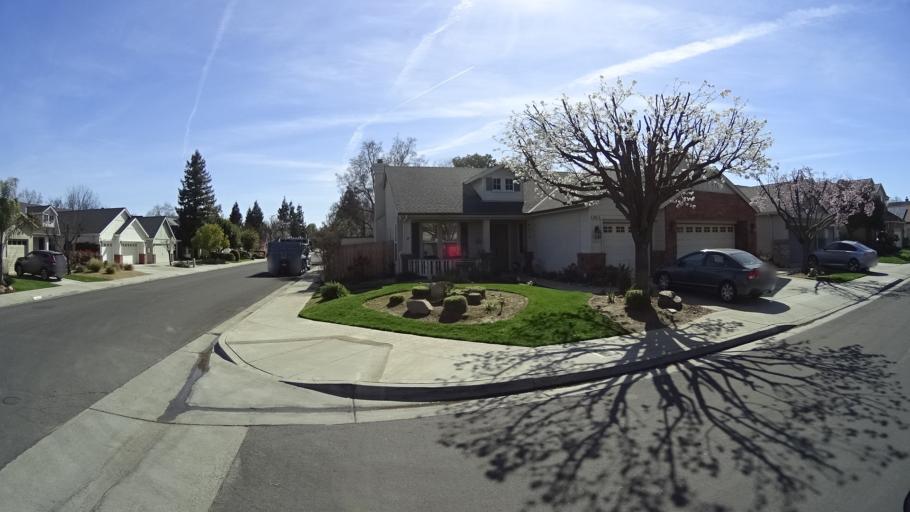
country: US
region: California
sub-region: Fresno County
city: Clovis
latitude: 36.8508
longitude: -119.7359
